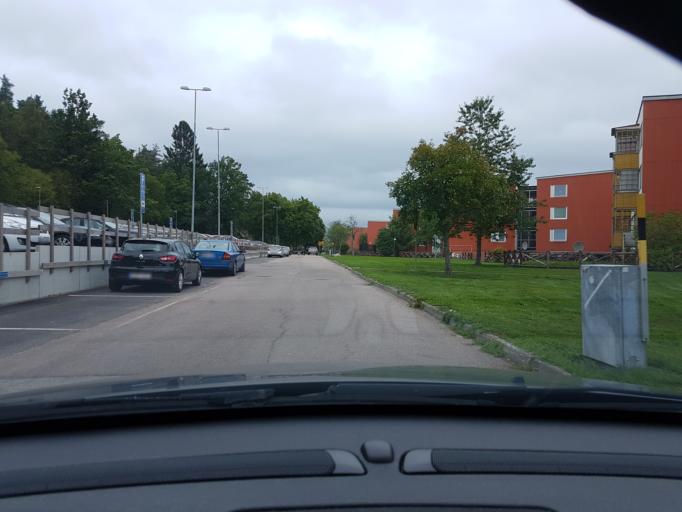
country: SE
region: Vaestra Goetaland
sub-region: Ale Kommun
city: Nodinge-Nol
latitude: 57.9129
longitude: 12.0668
